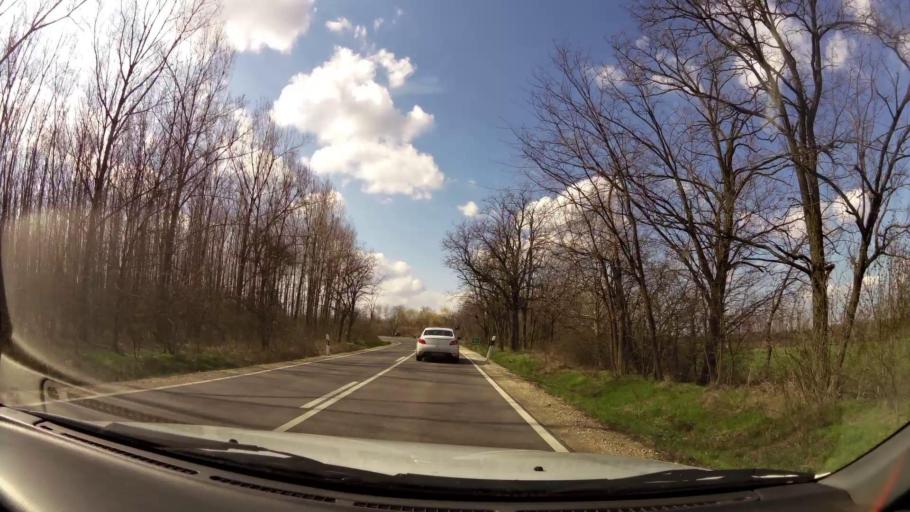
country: HU
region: Pest
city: Forropuszta
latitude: 47.4635
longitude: 19.6518
